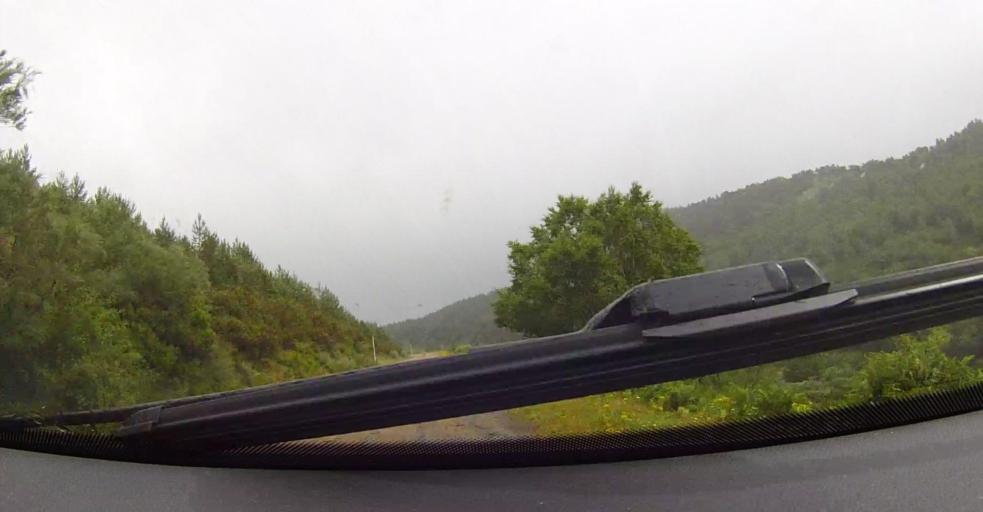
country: ES
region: Castille and Leon
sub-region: Provincia de Leon
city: Puebla de Lillo
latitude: 43.0749
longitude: -5.2523
